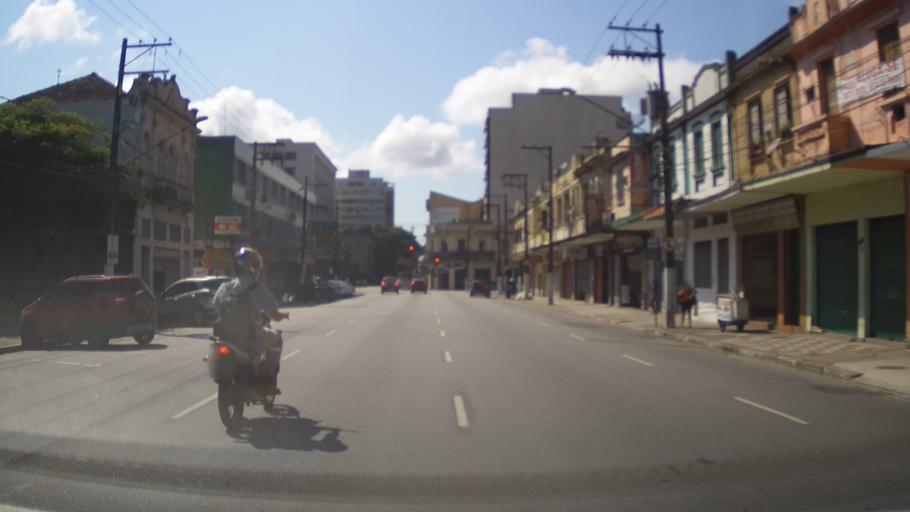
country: BR
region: Sao Paulo
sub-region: Santos
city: Santos
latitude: -23.9372
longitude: -46.3266
